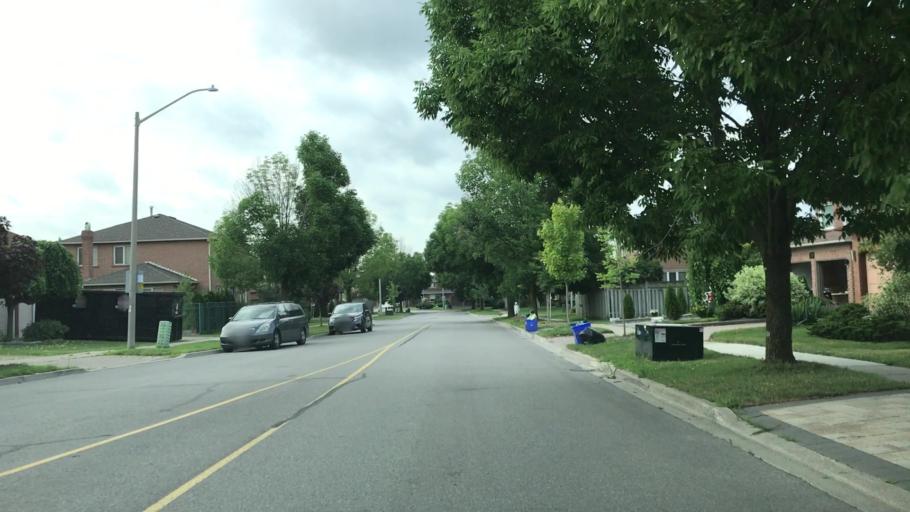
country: CA
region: Ontario
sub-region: York
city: Richmond Hill
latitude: 43.8581
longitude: -79.4026
